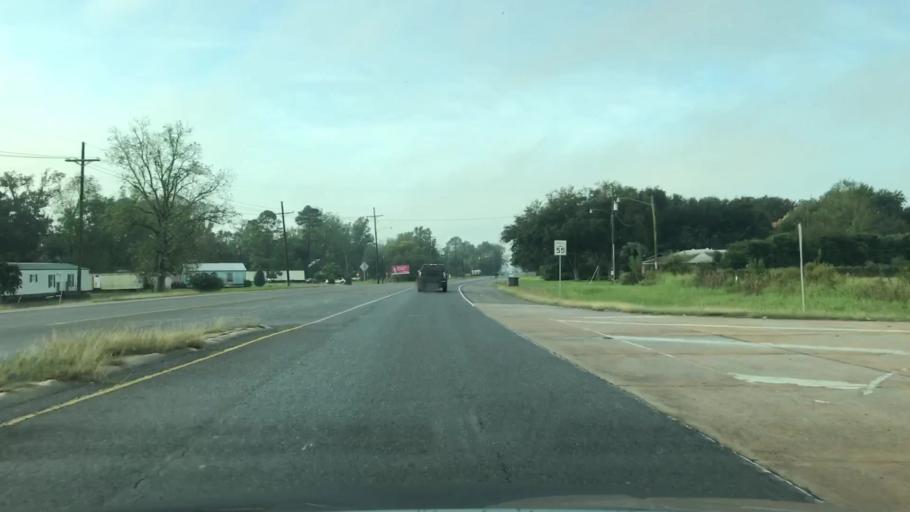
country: US
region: Louisiana
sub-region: Terrebonne Parish
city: Gray
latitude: 29.6765
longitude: -90.8135
